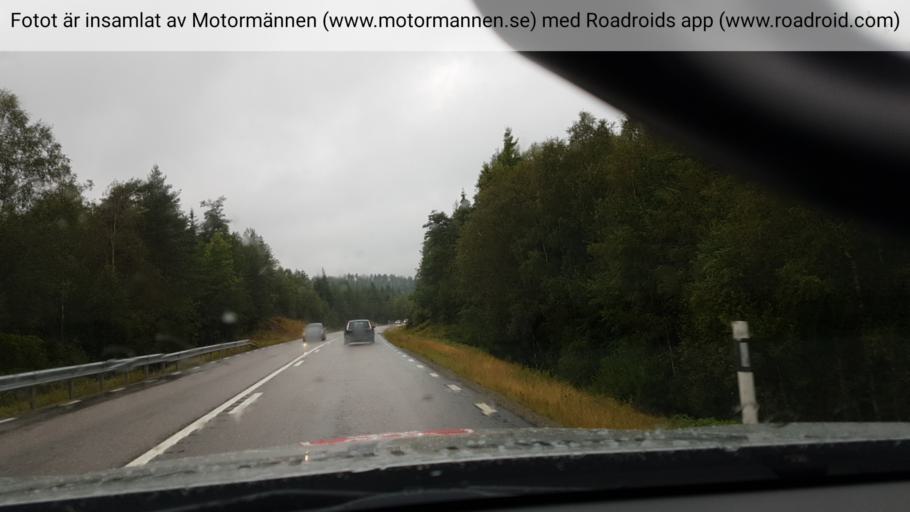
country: SE
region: Vaestra Goetaland
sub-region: Dals-Ed Kommun
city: Ed
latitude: 58.8729
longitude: 11.8435
